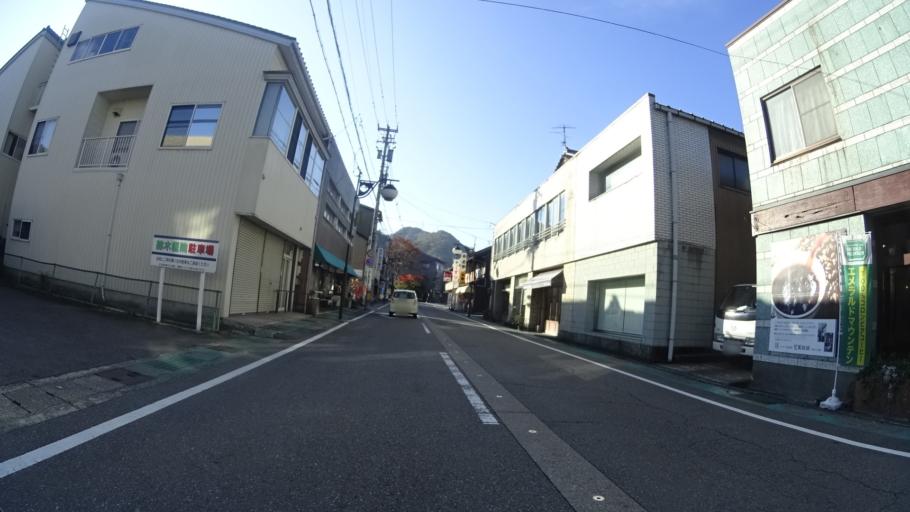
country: JP
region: Fukui
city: Maruoka
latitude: 36.2487
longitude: 136.3745
